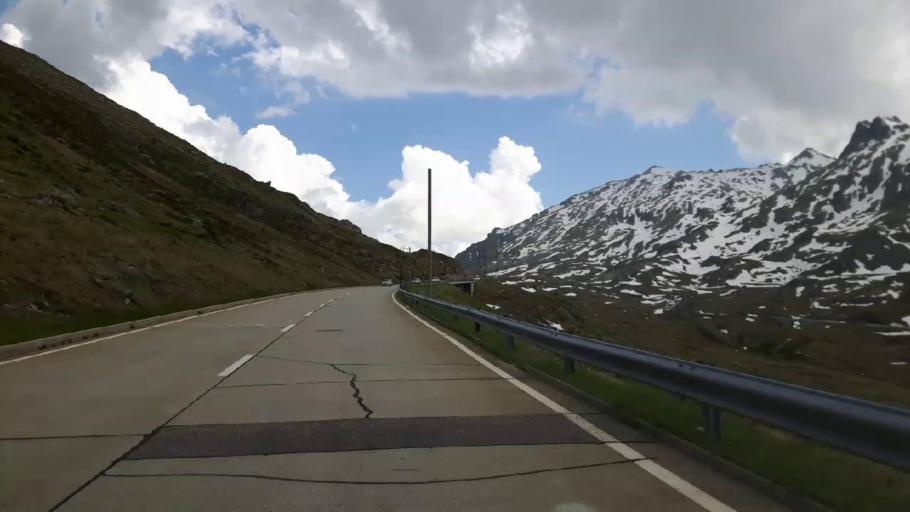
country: CH
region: Ticino
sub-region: Leventina District
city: Airolo
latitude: 46.5713
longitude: 8.5610
